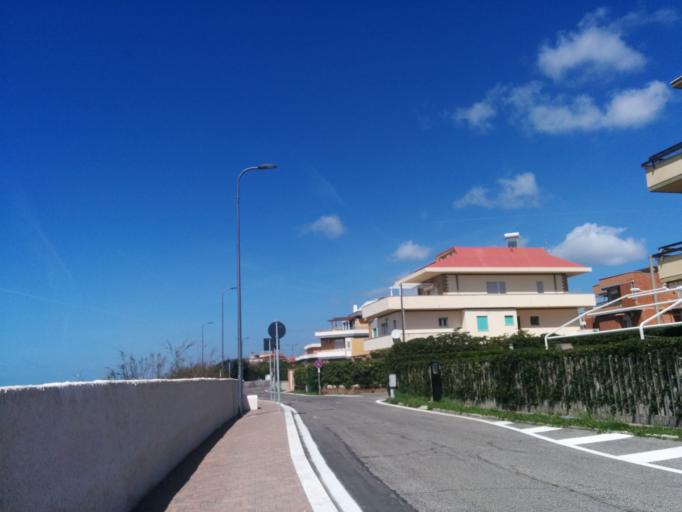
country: IT
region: Latium
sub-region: Citta metropolitana di Roma Capitale
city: Lavinio
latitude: 41.4954
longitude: 12.5865
